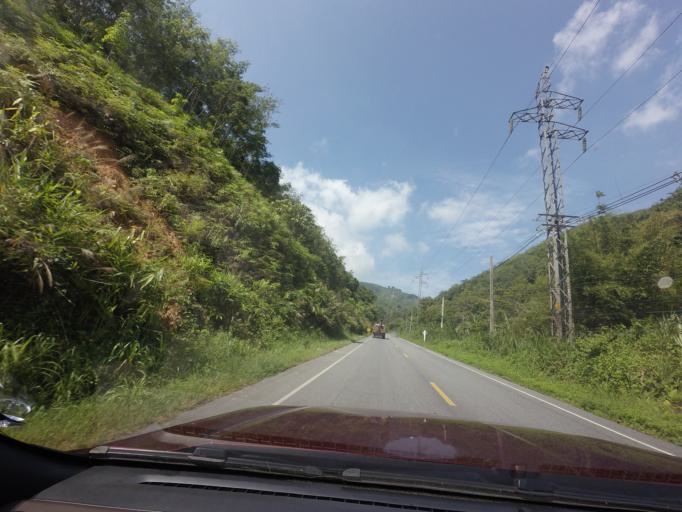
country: TH
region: Yala
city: Betong
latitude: 5.9175
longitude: 101.1574
